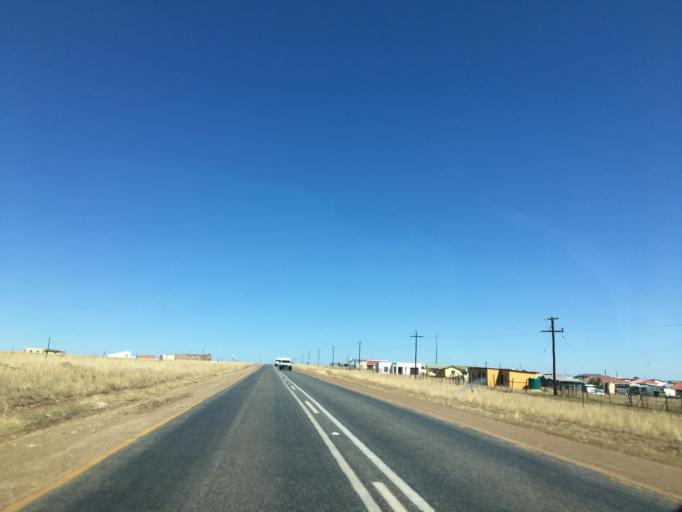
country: ZA
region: Eastern Cape
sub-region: Chris Hani District Municipality
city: Cofimvaba
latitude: -31.9247
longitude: 27.8377
